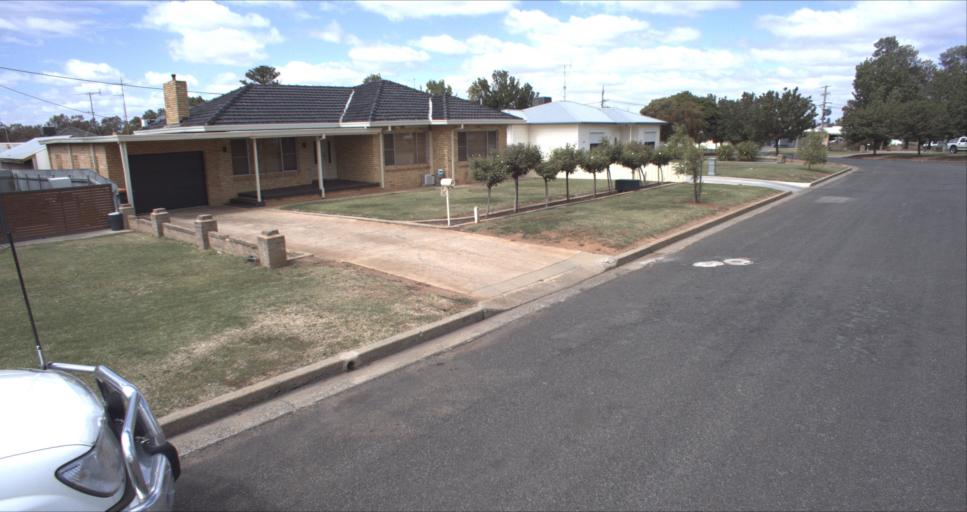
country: AU
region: New South Wales
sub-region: Leeton
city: Leeton
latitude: -34.5611
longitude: 146.3990
